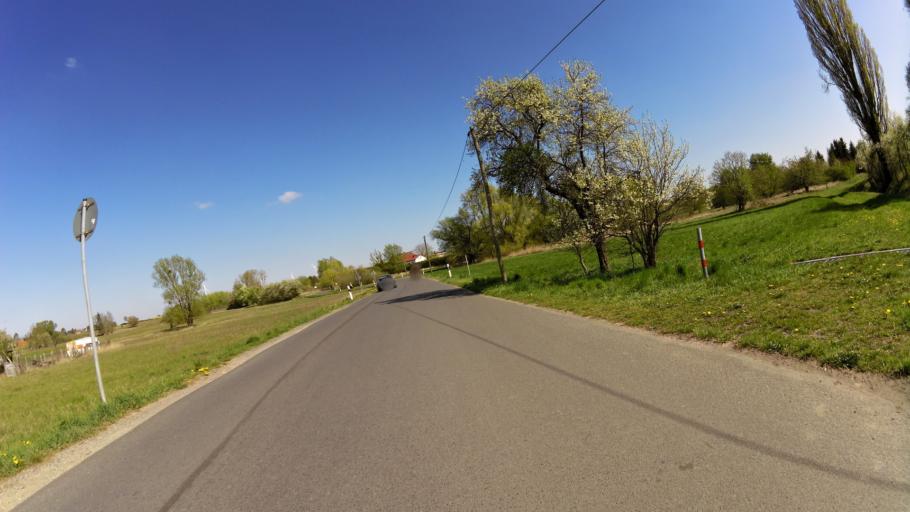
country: DE
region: Brandenburg
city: Muncheberg
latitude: 52.5099
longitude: 14.1398
